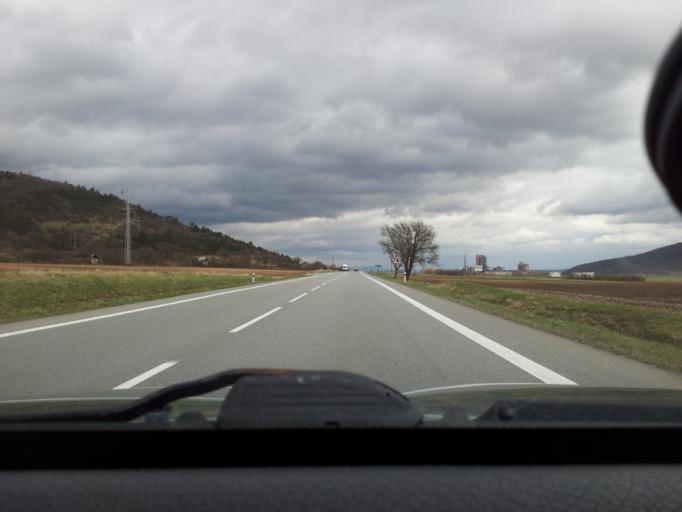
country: SK
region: Kosicky
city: Medzev
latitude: 48.6000
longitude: 20.8000
